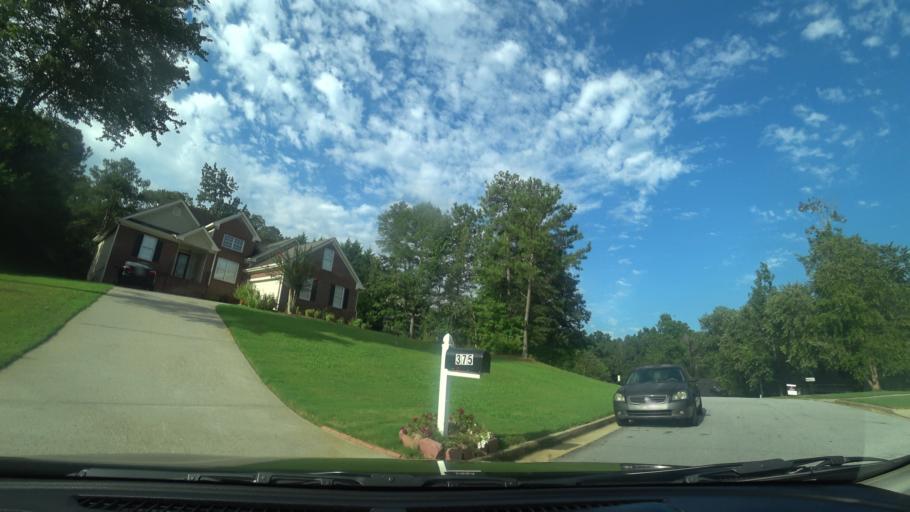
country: US
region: Georgia
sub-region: Newton County
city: Porterdale
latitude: 33.6213
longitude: -83.9534
